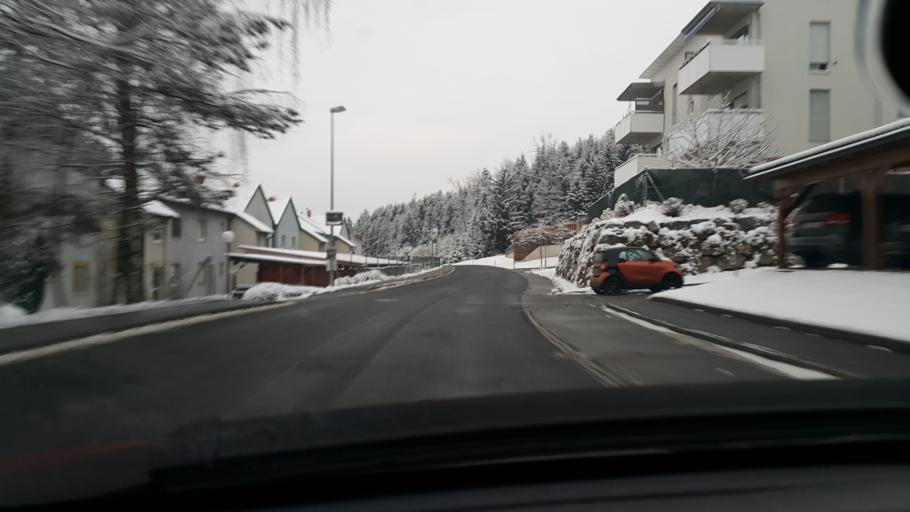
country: AT
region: Styria
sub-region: Politischer Bezirk Graz-Umgebung
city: Hitzendorf
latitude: 47.0558
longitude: 15.2852
